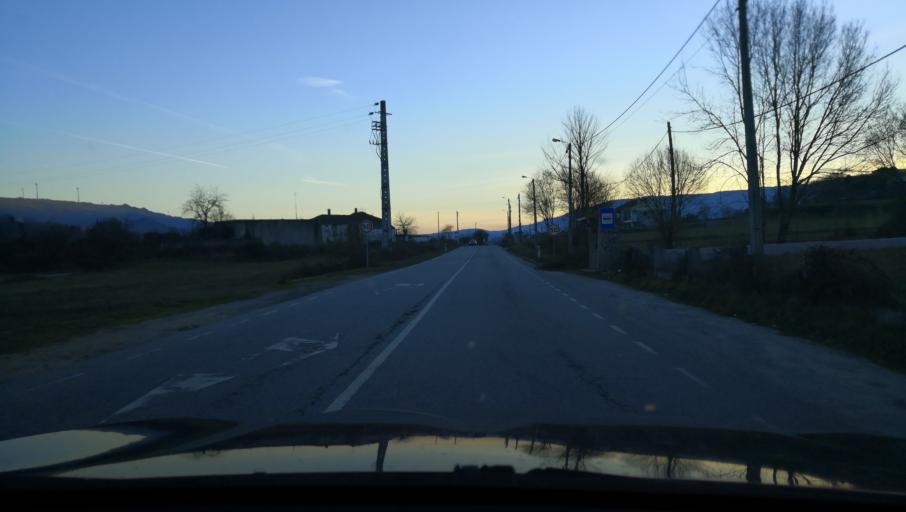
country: PT
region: Vila Real
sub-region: Vila Pouca de Aguiar
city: Vila Pouca de Aguiar
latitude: 41.4817
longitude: -7.6543
